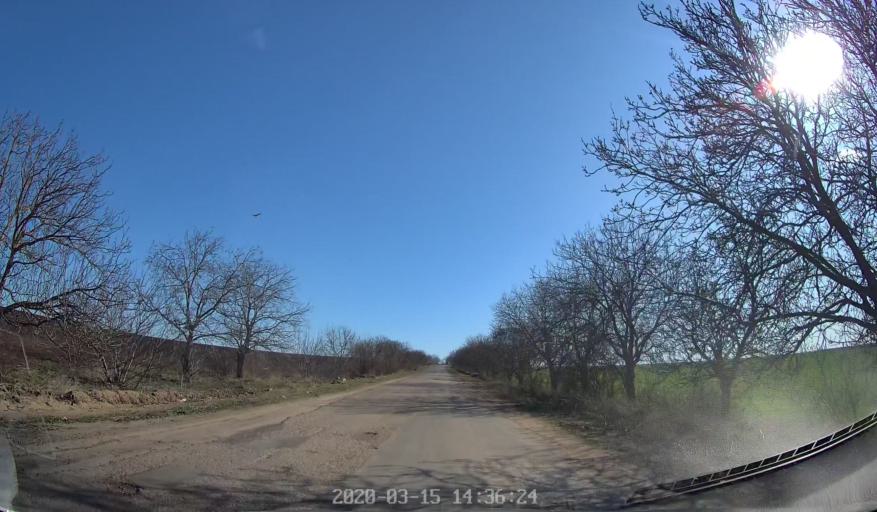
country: MD
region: Orhei
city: Orhei
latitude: 47.3256
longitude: 28.9253
